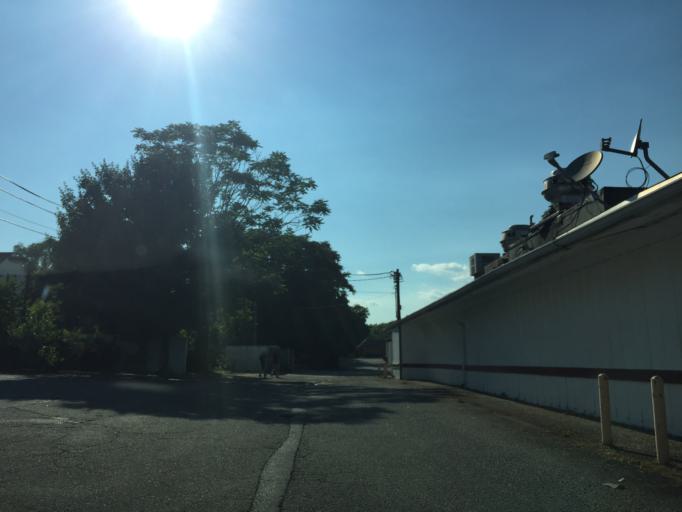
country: US
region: Maryland
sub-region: Baltimore County
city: Rosedale
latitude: 39.2912
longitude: -76.5114
